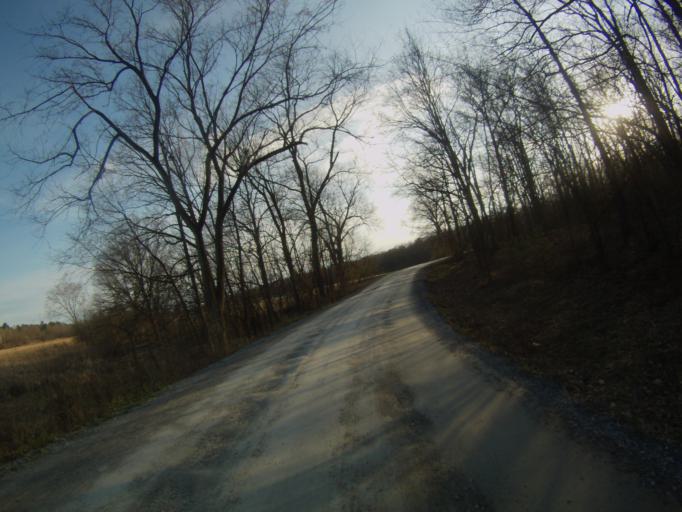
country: US
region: New York
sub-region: Essex County
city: Port Henry
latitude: 44.0760
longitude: -73.3503
